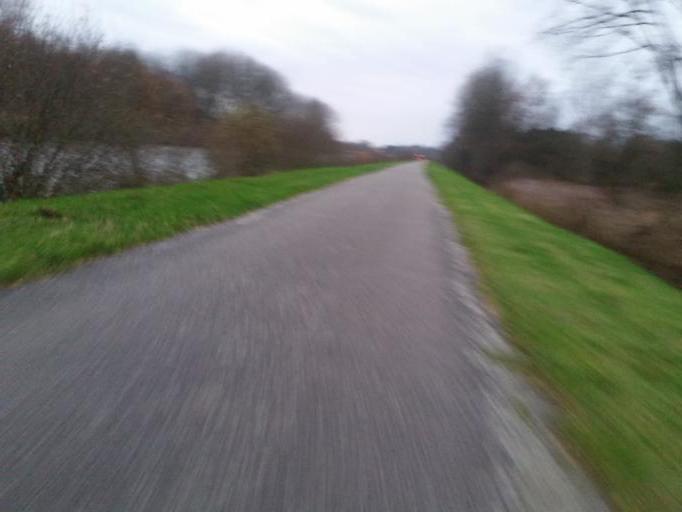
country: BE
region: Flanders
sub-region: Provincie Antwerpen
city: Lier
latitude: 51.1558
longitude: 4.5974
